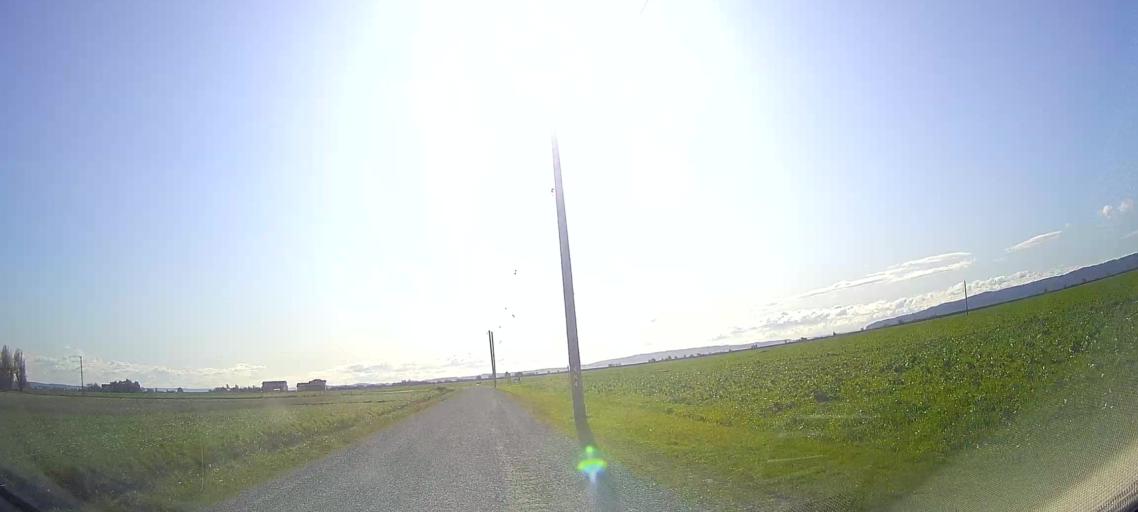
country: US
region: Washington
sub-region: Skagit County
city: Mount Vernon
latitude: 48.3571
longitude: -122.4488
